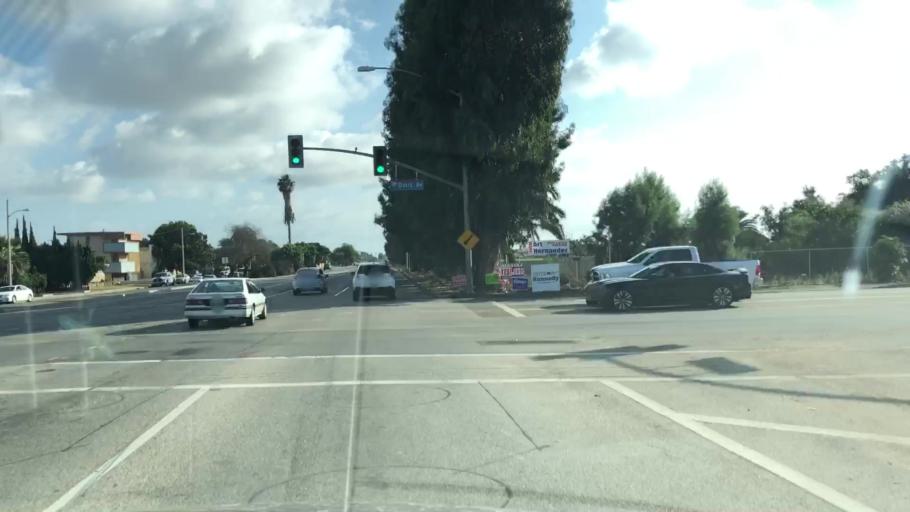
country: US
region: California
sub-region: Ventura County
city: Oxnard
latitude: 34.2085
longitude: -119.1948
